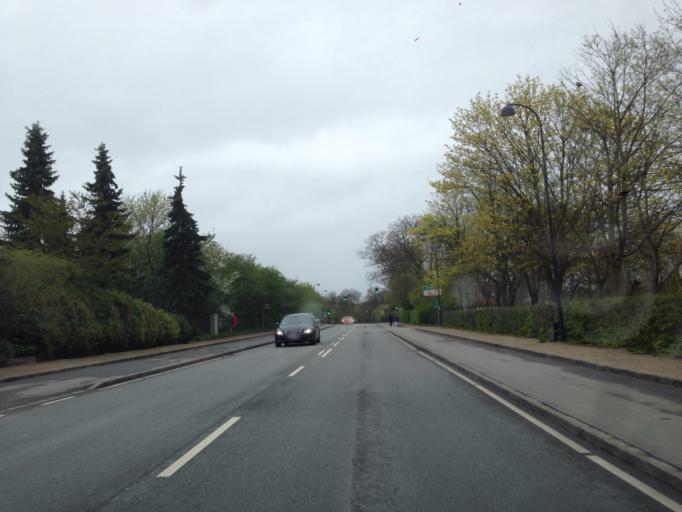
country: DK
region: Capital Region
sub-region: Rudersdal Kommune
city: Trorod
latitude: 55.8460
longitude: 12.5278
